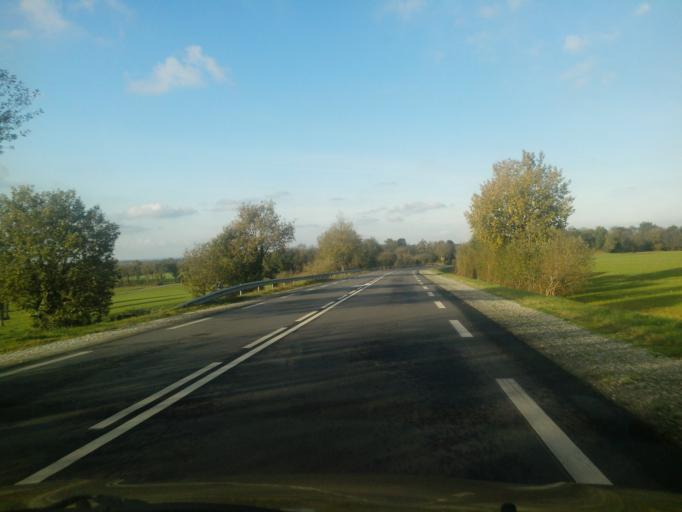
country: FR
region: Brittany
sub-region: Departement du Morbihan
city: Mauron
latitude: 48.0397
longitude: -2.3034
